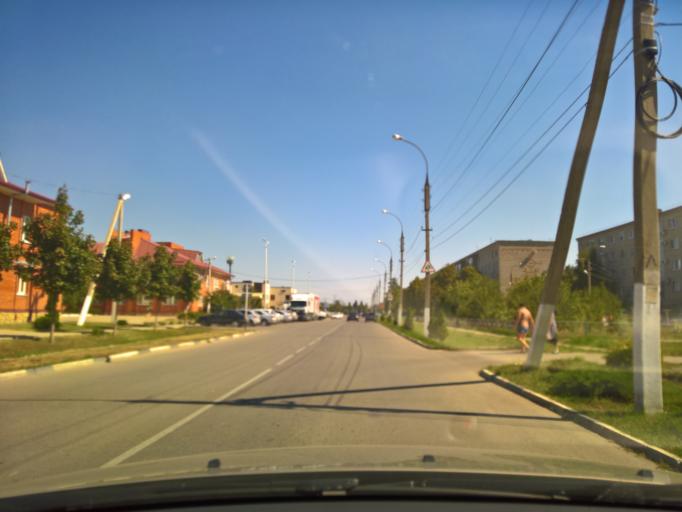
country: RU
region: Krasnodarskiy
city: Slavyansk-na-Kubani
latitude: 45.2657
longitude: 38.1055
